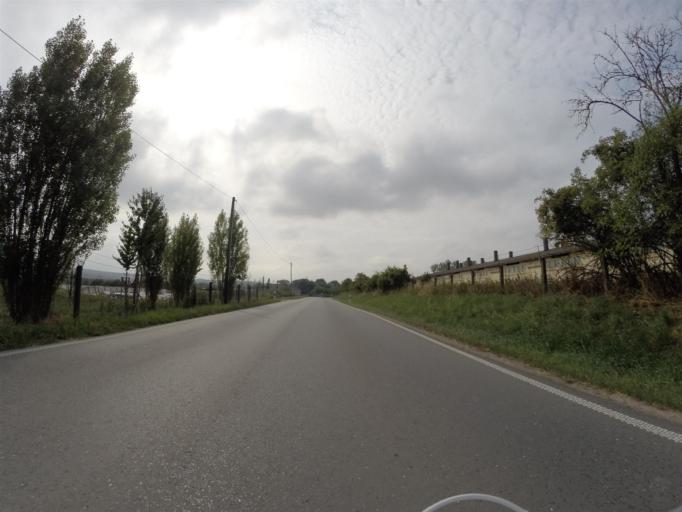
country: DE
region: Thuringia
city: Schongleina
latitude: 50.9222
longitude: 11.7304
